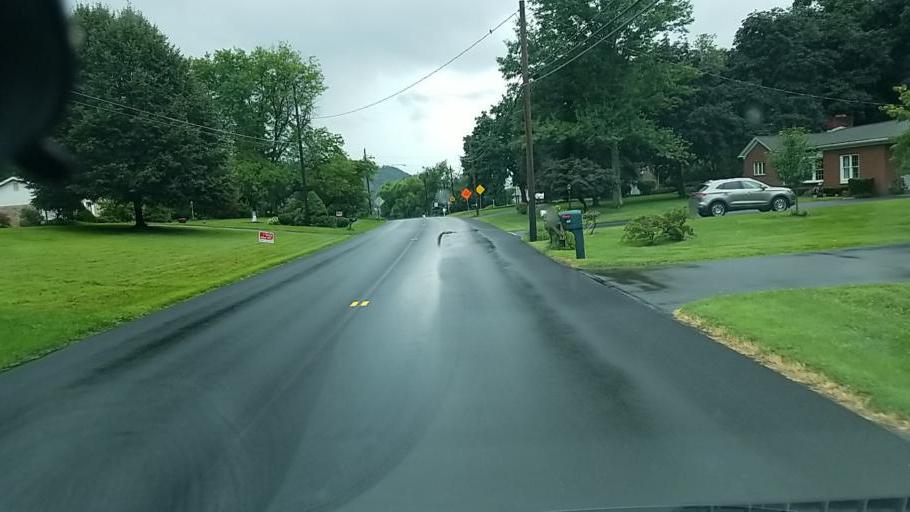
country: US
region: Pennsylvania
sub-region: Dauphin County
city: Millersburg
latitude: 40.5468
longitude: -76.9477
